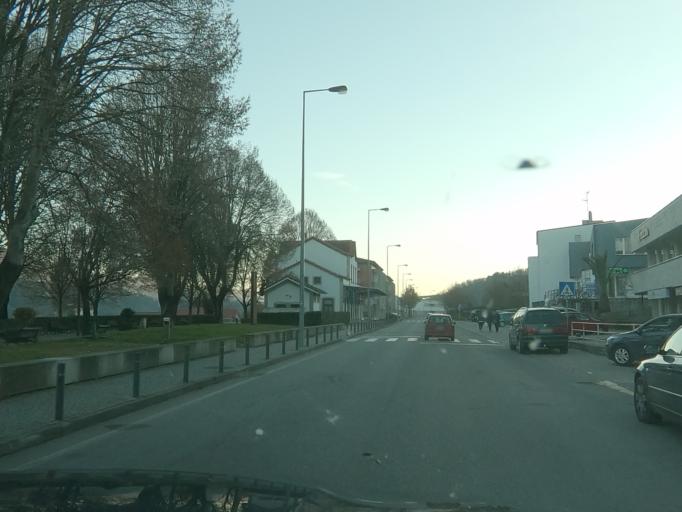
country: PT
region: Vila Real
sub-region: Vila Pouca de Aguiar
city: Vila Pouca de Aguiar
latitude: 41.5008
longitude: -7.6464
